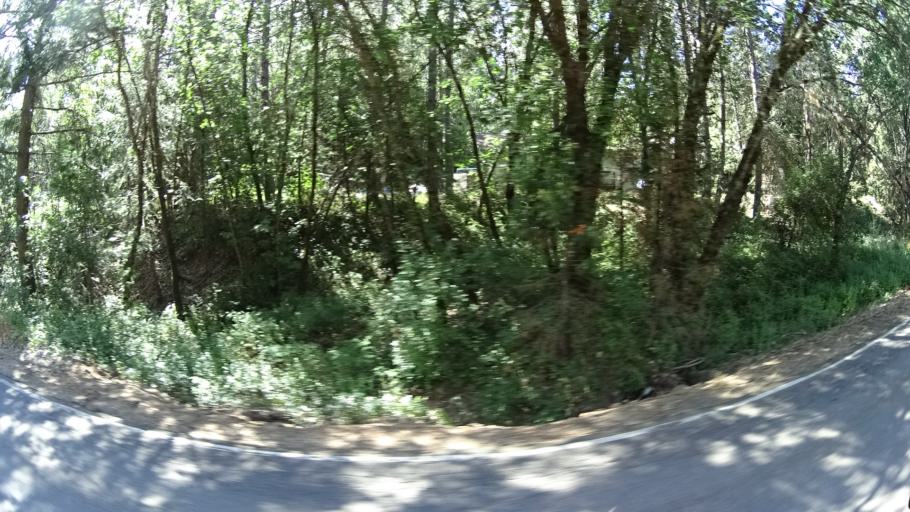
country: US
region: California
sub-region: Amador County
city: Pioneer
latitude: 38.3519
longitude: -120.5101
